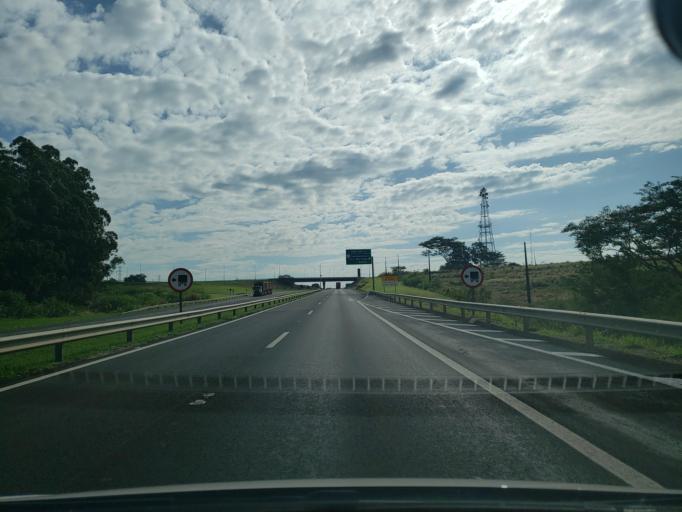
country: BR
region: Sao Paulo
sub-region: Lins
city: Lins
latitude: -21.6681
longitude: -49.7860
